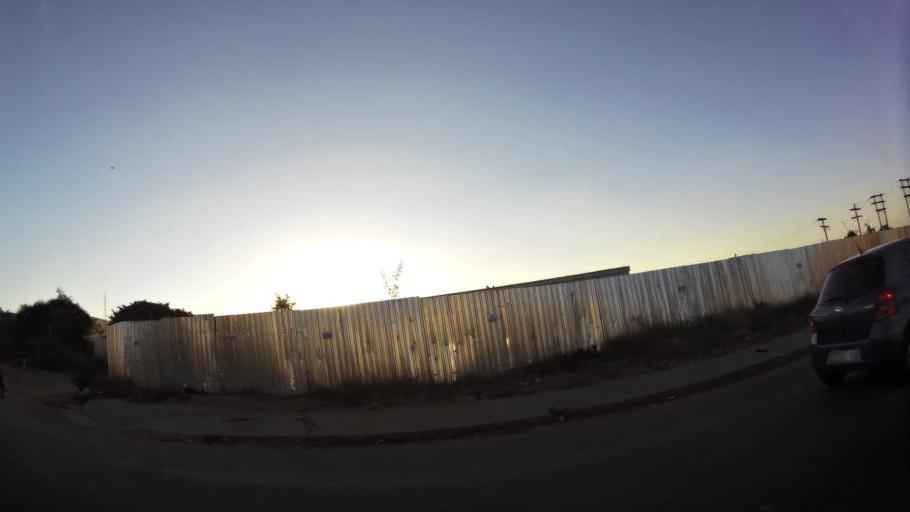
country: ZA
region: North-West
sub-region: Bojanala Platinum District Municipality
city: Rustenburg
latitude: -25.6474
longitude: 27.2153
